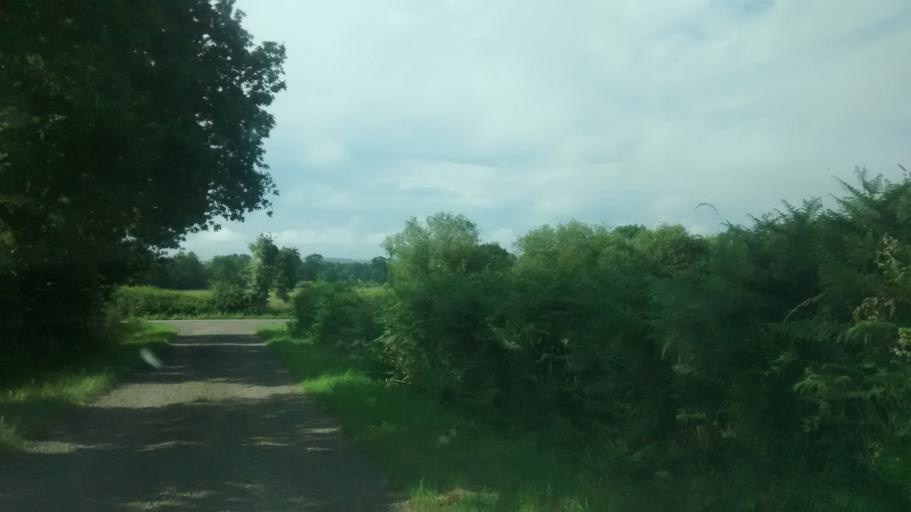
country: FR
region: Brittany
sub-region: Departement d'Ille-et-Vilaine
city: Plechatel
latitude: 47.8458
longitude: -1.7412
